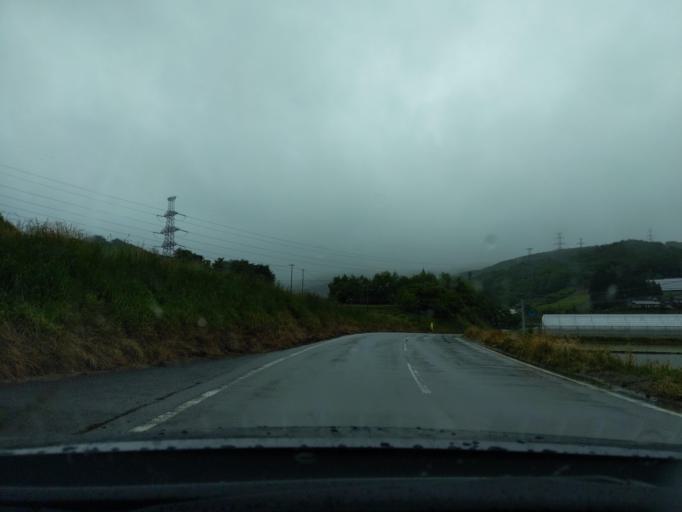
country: JP
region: Fukushima
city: Funehikimachi-funehiki
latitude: 37.6099
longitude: 140.6543
